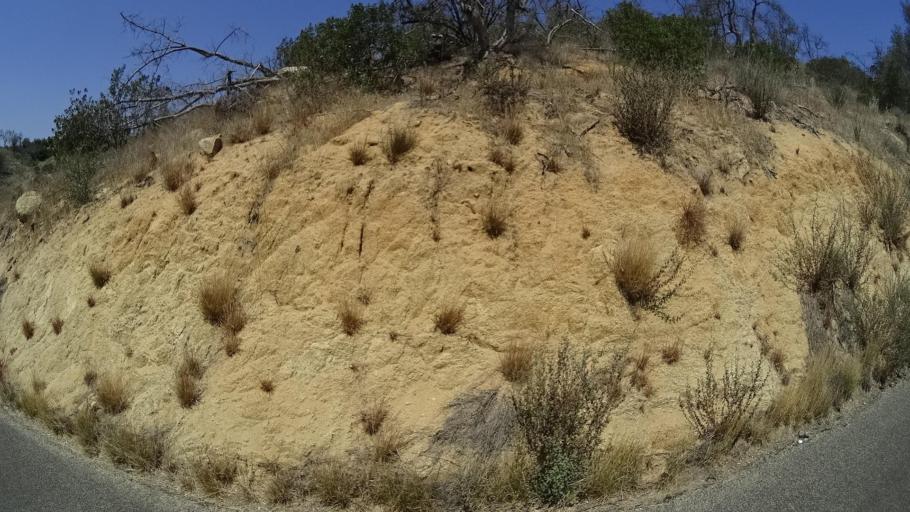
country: US
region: California
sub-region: San Diego County
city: Fallbrook
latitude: 33.4484
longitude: -117.2853
